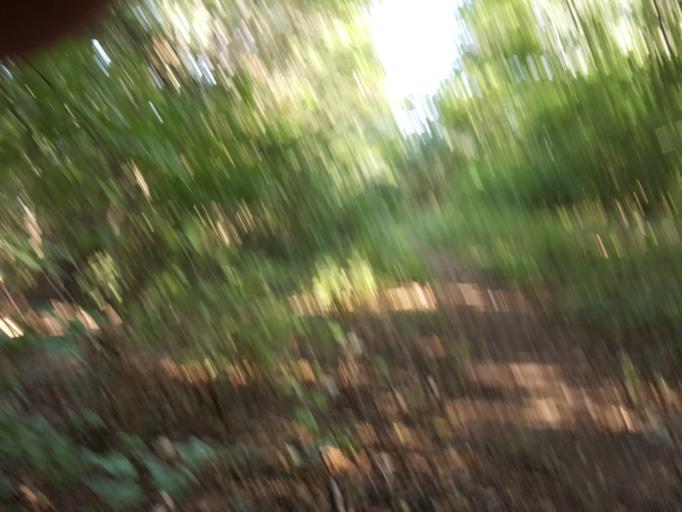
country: DE
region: Lower Saxony
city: Nienburg
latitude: 52.6477
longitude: 9.2394
